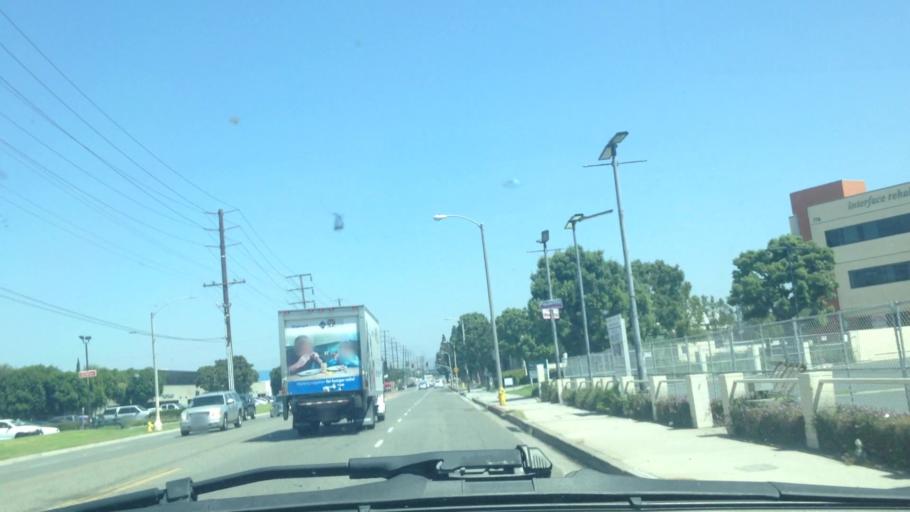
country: US
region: California
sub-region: Orange County
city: Placentia
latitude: 33.8609
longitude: -117.8827
